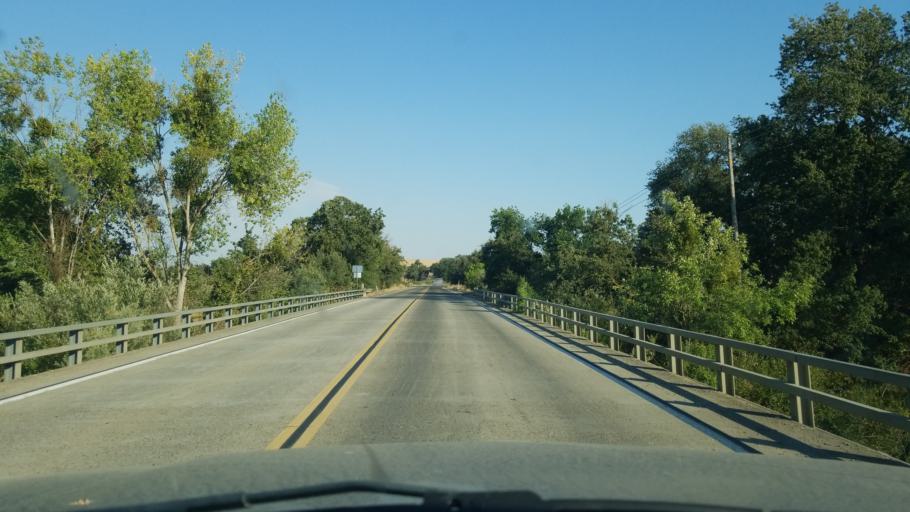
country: US
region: California
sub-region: Merced County
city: Winton
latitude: 37.5053
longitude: -120.4513
